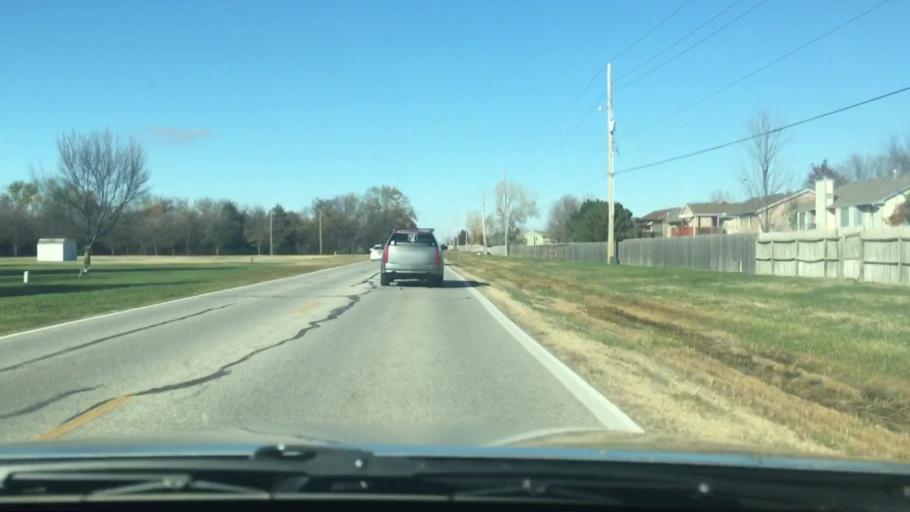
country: US
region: Kansas
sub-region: Sedgwick County
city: Maize
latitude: 37.7278
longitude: -97.4810
